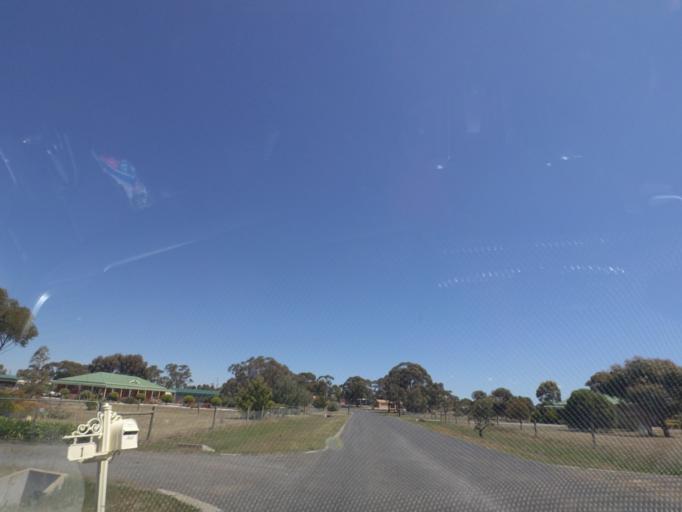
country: AU
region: Victoria
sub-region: Melton
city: Brookfield
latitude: -37.6961
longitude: 144.4997
